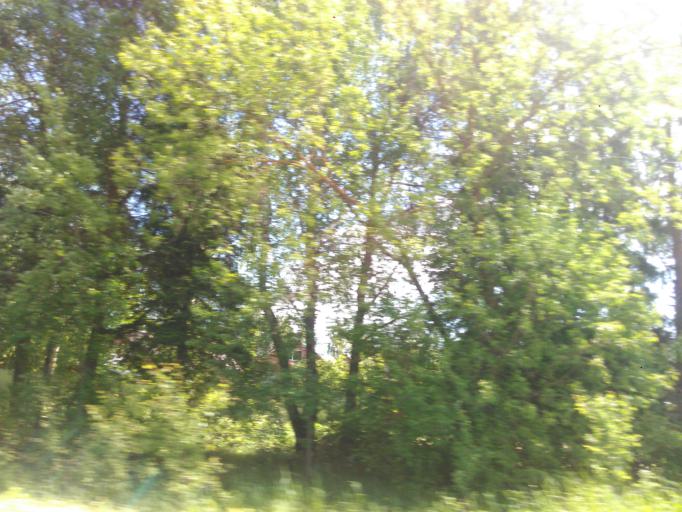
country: RU
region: Moskovskaya
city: Solnechnogorsk
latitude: 56.0808
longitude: 36.9091
